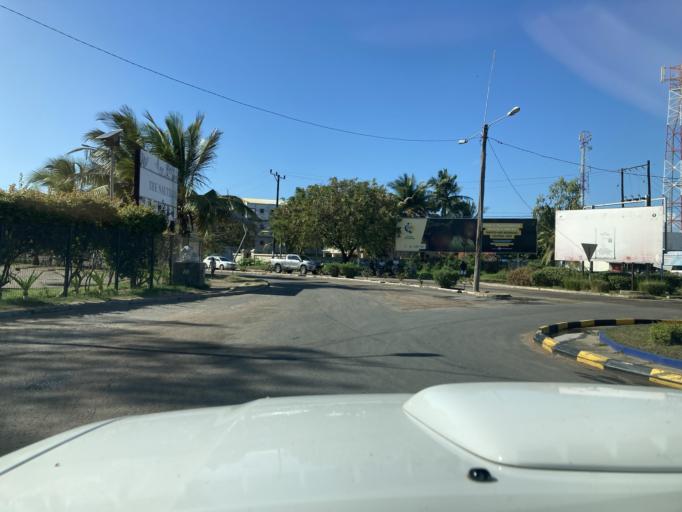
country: MZ
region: Cabo Delgado
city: Pemba
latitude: -12.9722
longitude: 40.5403
